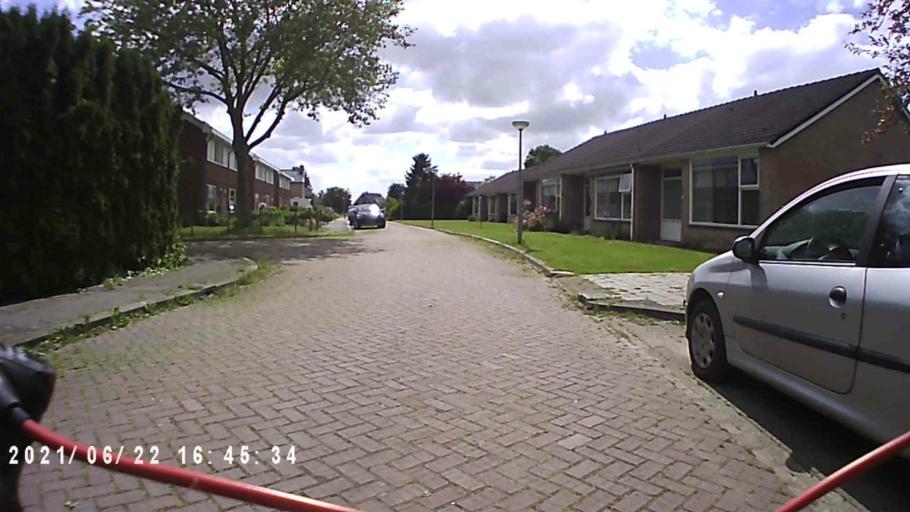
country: NL
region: Groningen
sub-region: Gemeente Bedum
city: Bedum
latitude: 53.3456
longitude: 6.6384
